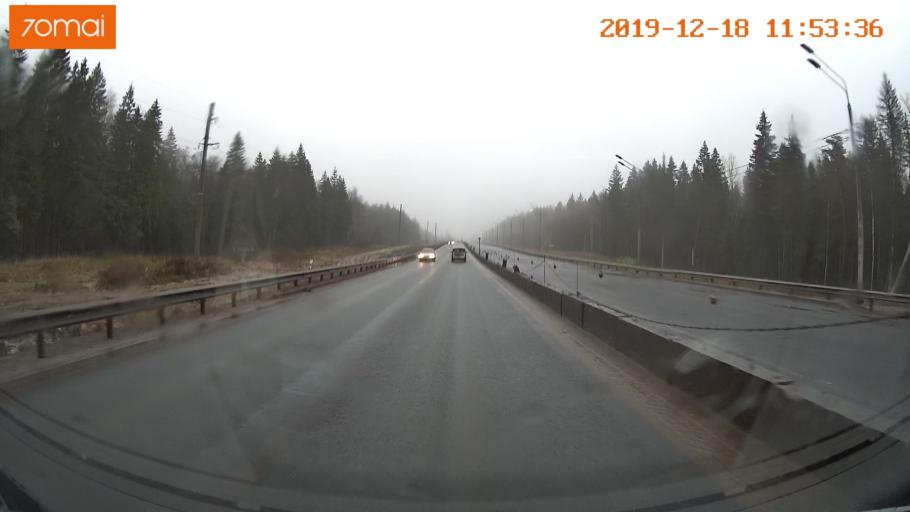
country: RU
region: Moskovskaya
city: Yershovo
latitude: 55.8062
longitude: 36.9197
